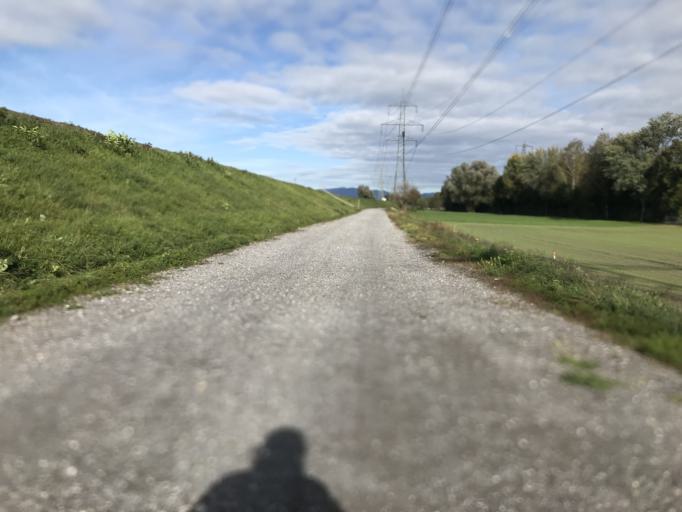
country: AT
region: Vorarlberg
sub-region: Politischer Bezirk Feldkirch
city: Mader
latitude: 47.3509
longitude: 9.6068
